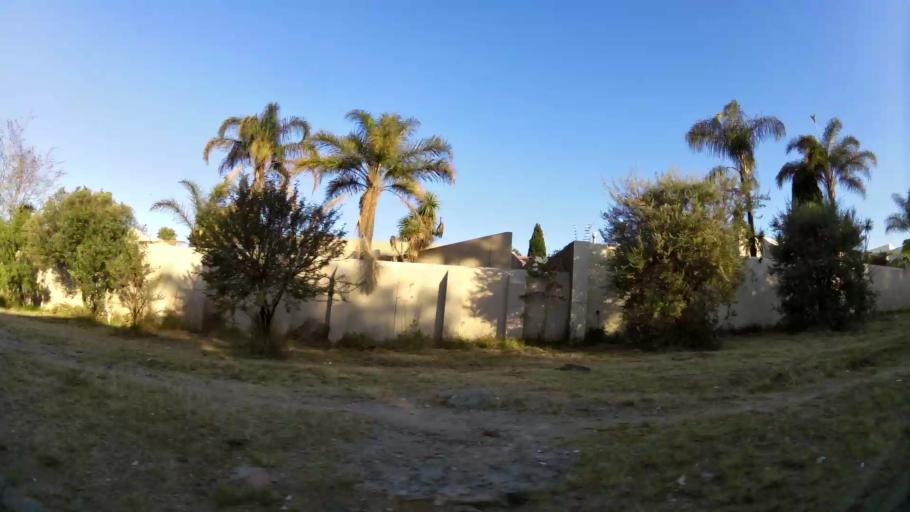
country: ZA
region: Gauteng
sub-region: City of Johannesburg Metropolitan Municipality
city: Modderfontein
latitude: -26.0727
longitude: 28.0629
